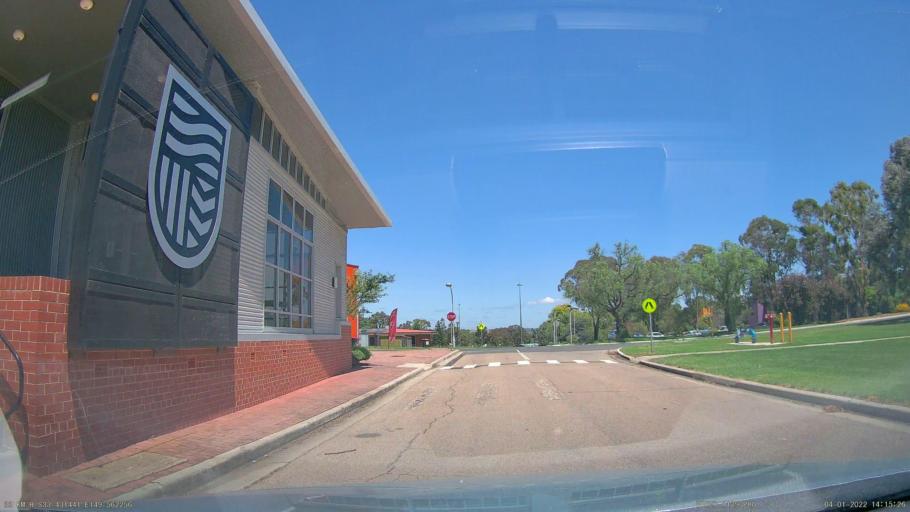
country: AU
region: New South Wales
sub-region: Bathurst Regional
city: Bathurst
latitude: -33.4315
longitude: 149.5623
